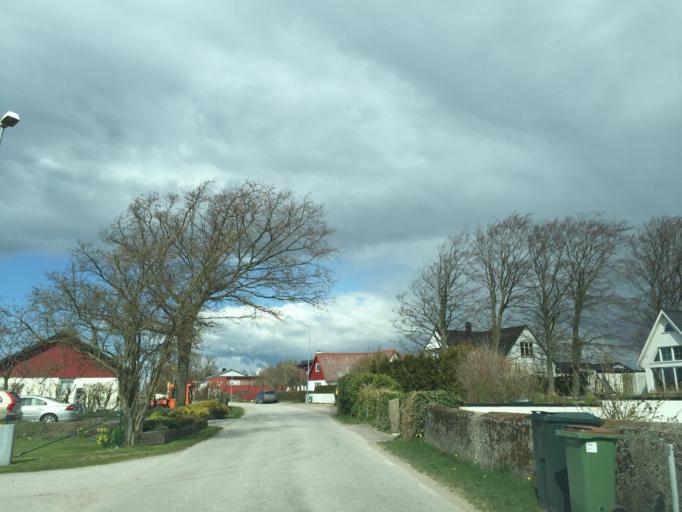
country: SE
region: Skane
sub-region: Vellinge Kommun
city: Hollviken
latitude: 55.4355
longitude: 12.9550
